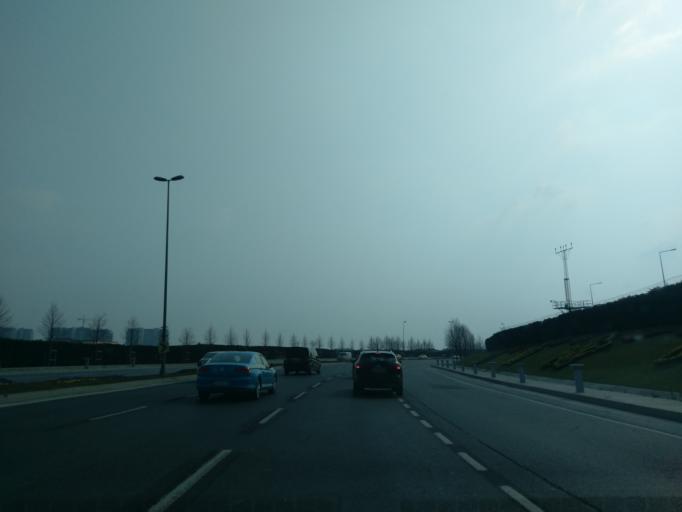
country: TR
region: Istanbul
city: Bahcelievler
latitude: 40.9806
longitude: 28.8406
